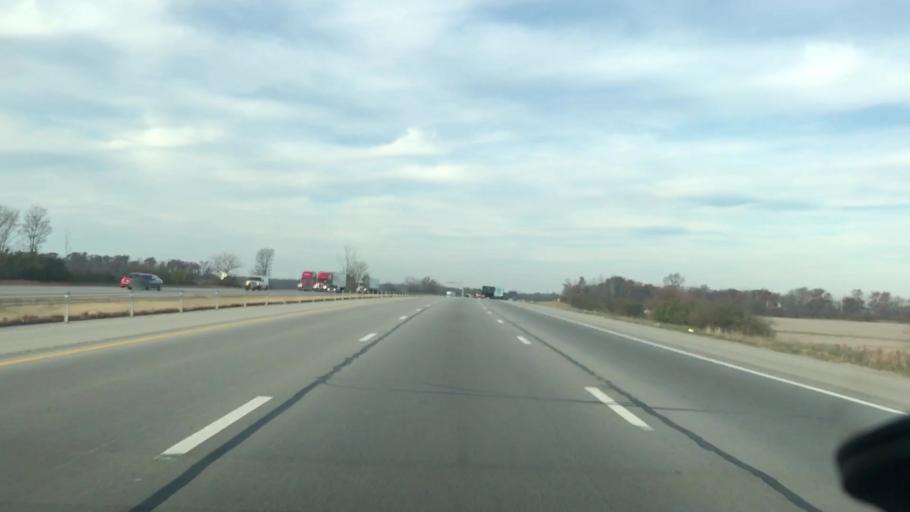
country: US
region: Ohio
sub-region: Clark County
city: Enon
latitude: 39.8922
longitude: -83.8813
